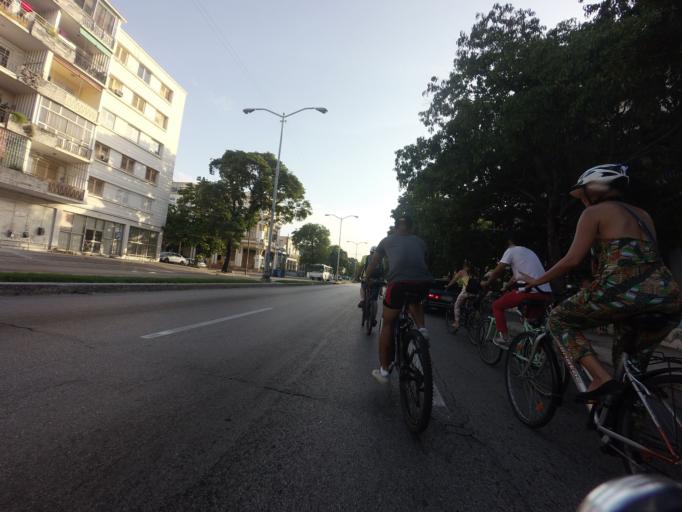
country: CU
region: La Habana
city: Havana
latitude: 23.1327
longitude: -82.4056
